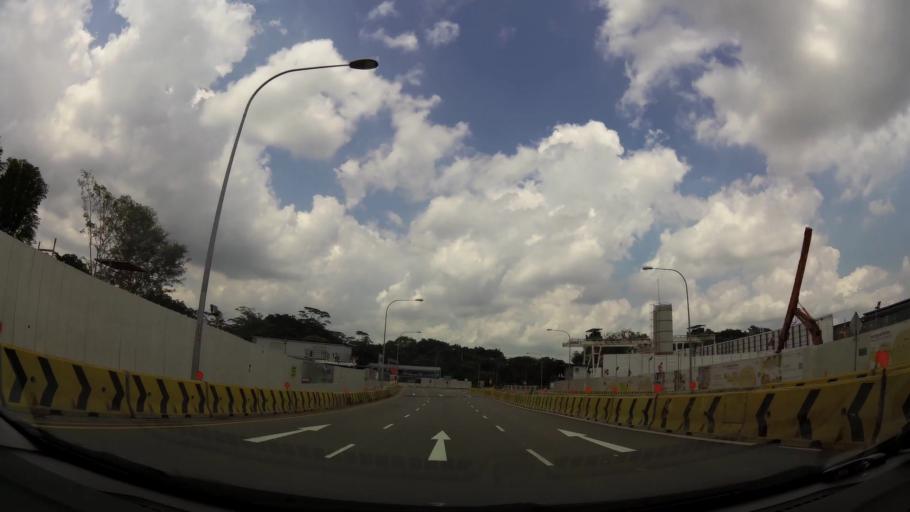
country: MY
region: Johor
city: Johor Bahru
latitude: 1.3983
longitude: 103.8175
